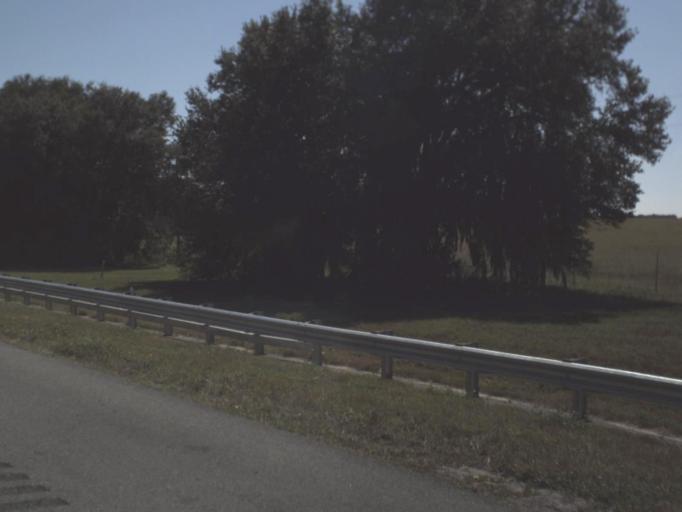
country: US
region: Florida
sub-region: Lake County
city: Leesburg
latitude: 28.7782
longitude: -81.9672
